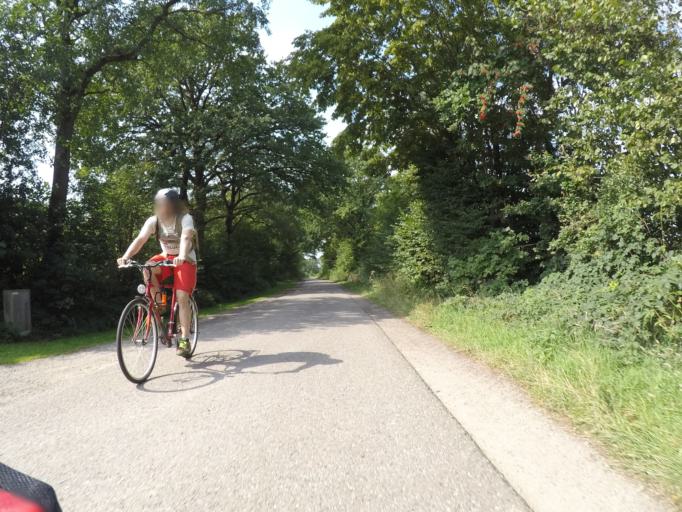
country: DE
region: Schleswig-Holstein
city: Kisdorf
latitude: 53.7798
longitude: 10.0249
